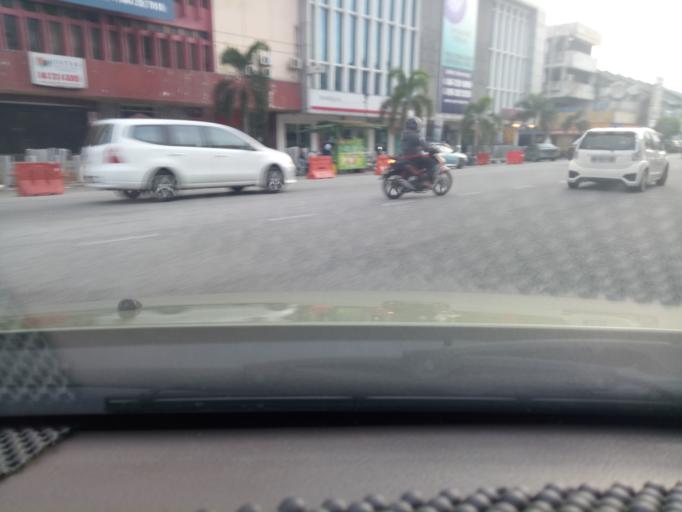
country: MY
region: Kedah
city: Alor Setar
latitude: 6.1167
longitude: 100.3687
